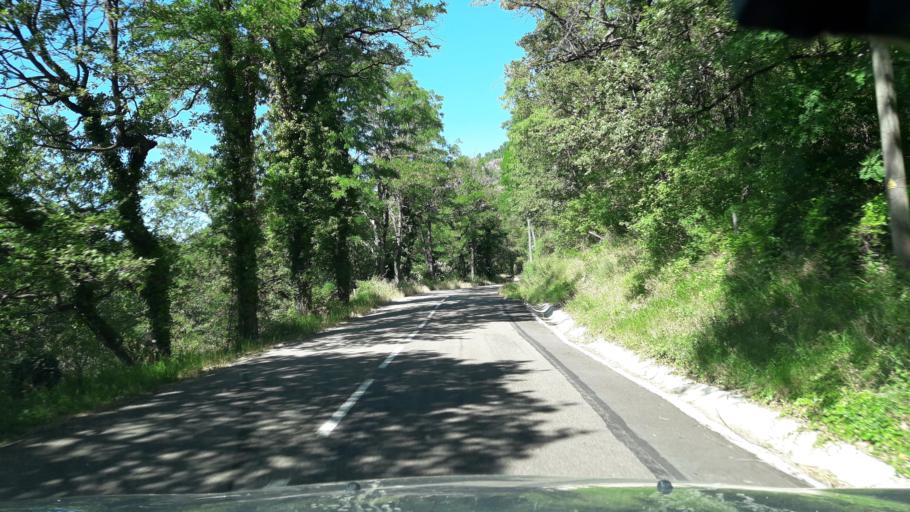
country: FR
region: Rhone-Alpes
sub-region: Departement de l'Ardeche
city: Villeneuve-de-Berg
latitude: 44.6127
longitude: 4.5395
